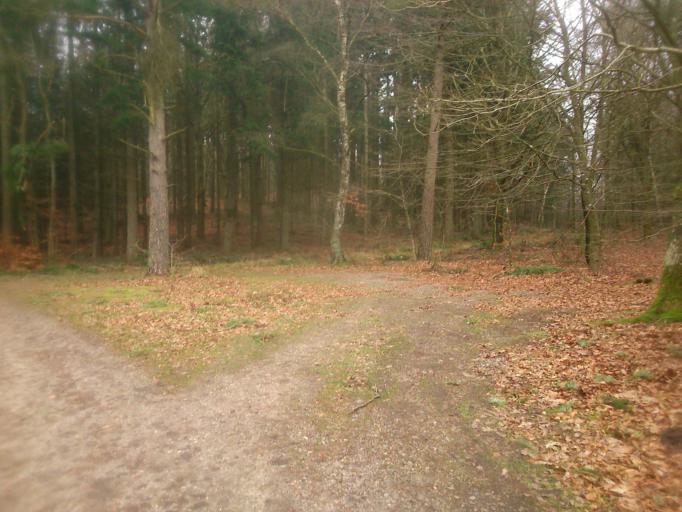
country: DK
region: Central Jutland
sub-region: Viborg Kommune
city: Bjerringbro
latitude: 56.3871
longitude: 9.7135
